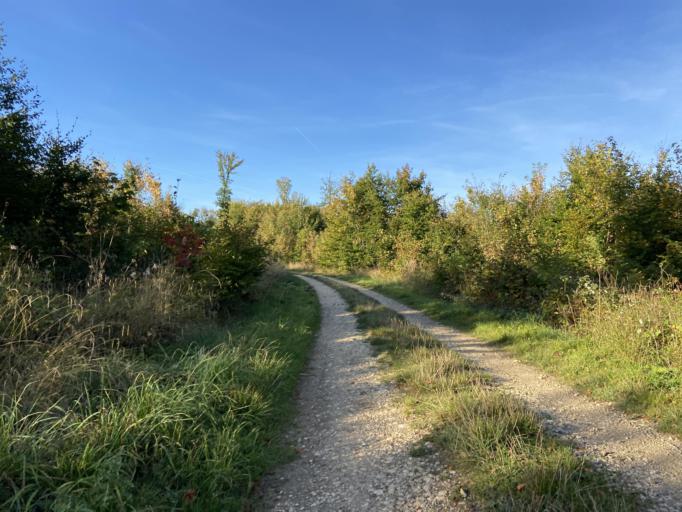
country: DE
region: Baden-Wuerttemberg
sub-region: Tuebingen Region
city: Bingen
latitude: 48.1239
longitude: 9.2994
